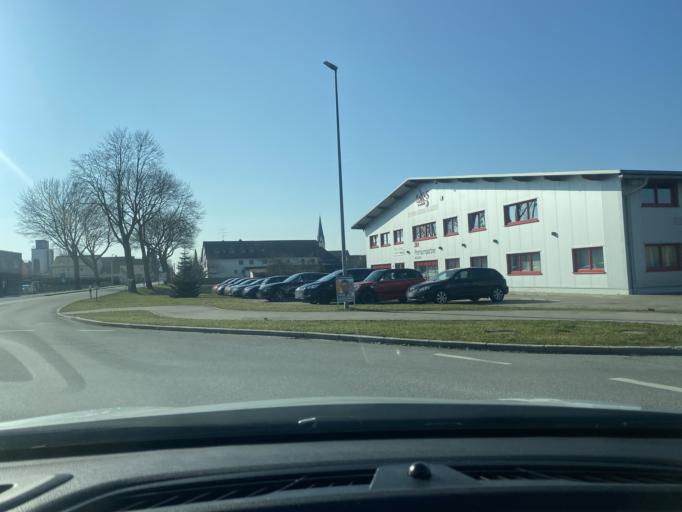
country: DE
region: Bavaria
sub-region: Upper Bavaria
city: Oberding
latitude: 48.3263
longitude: 11.8439
